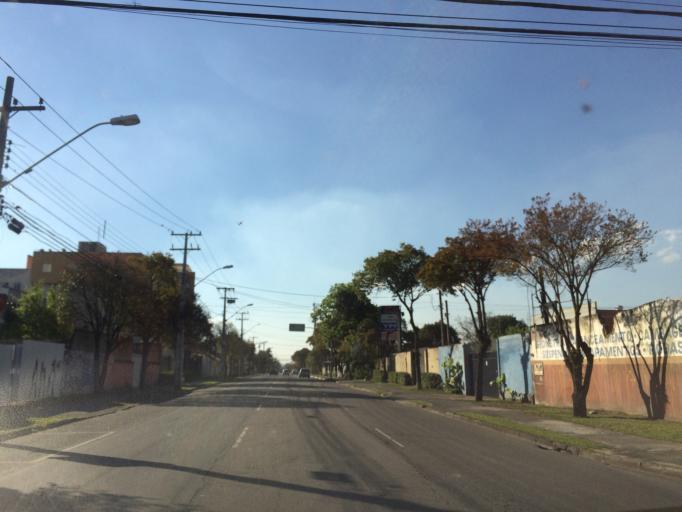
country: BR
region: Parana
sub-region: Sao Jose Dos Pinhais
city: Sao Jose dos Pinhais
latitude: -25.4881
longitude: -49.2428
